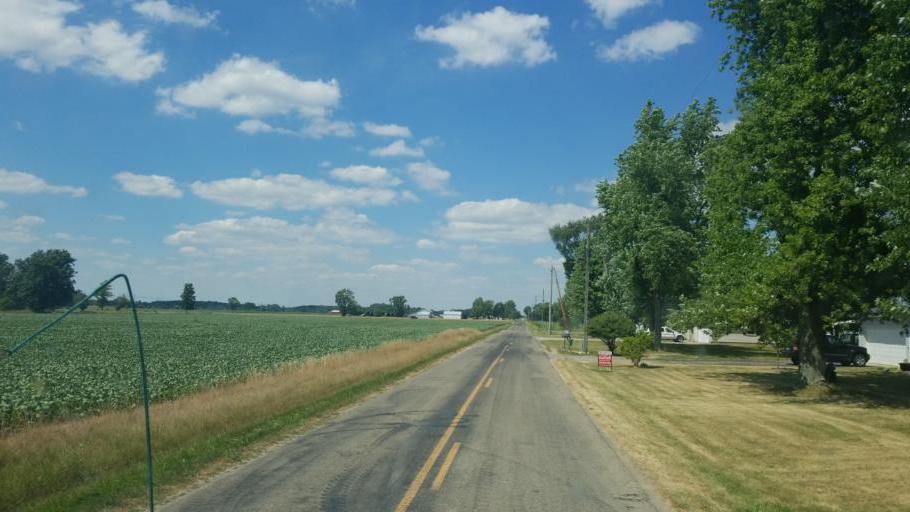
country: US
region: Ohio
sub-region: Defiance County
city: Hicksville
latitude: 41.3109
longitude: -84.7283
